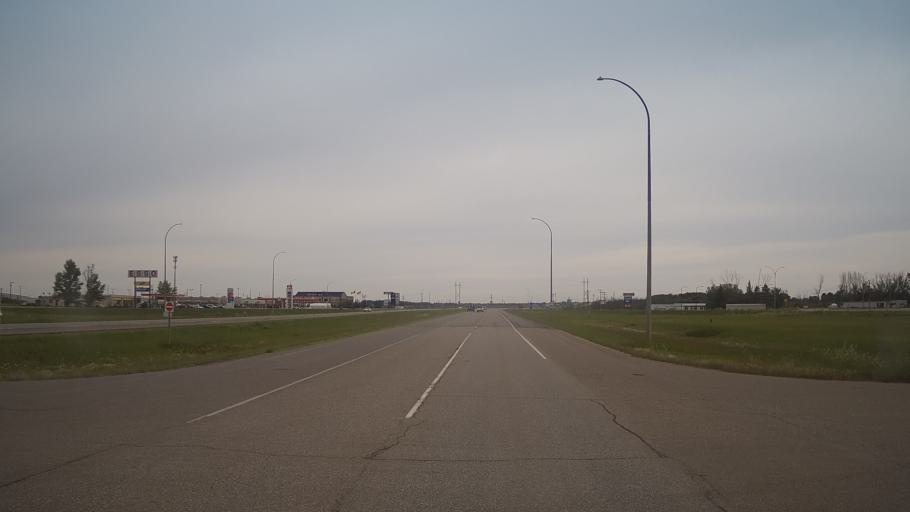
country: CA
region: Saskatchewan
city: Saskatoon
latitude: 52.0538
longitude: -106.5972
